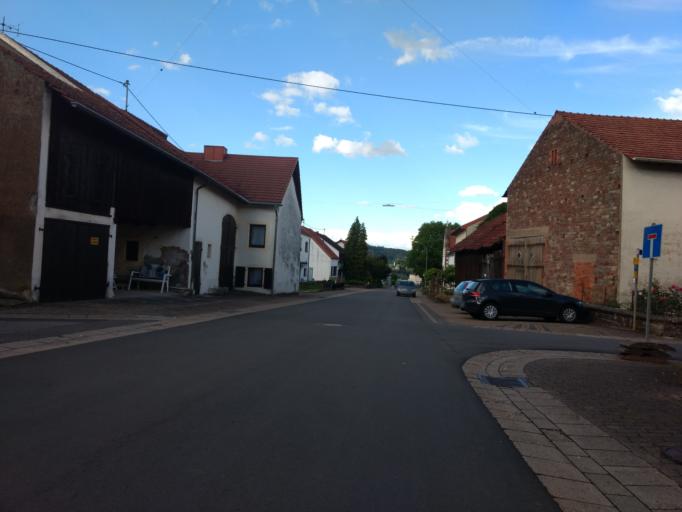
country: DE
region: Saarland
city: Merzig
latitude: 49.4437
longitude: 6.5968
